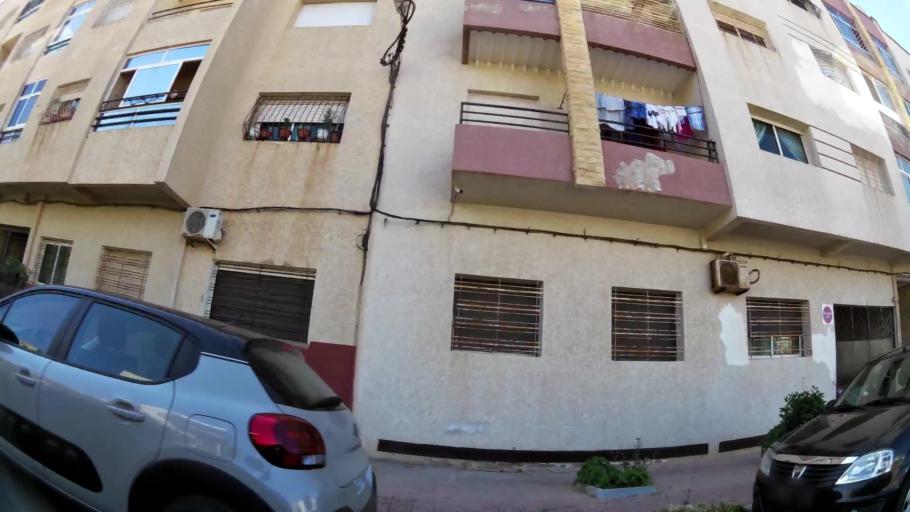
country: MA
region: Rabat-Sale-Zemmour-Zaer
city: Sale
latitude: 34.0714
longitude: -6.7993
